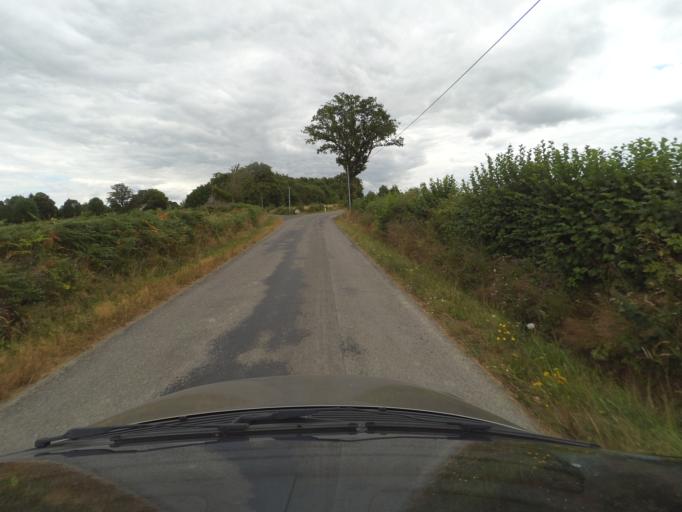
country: FR
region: Limousin
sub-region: Departement de la Haute-Vienne
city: Arnac-la-Poste
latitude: 46.2721
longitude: 1.2808
